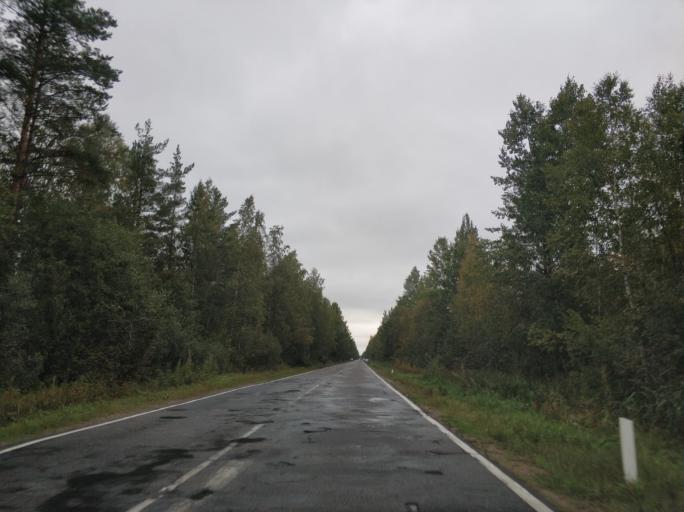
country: RU
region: Leningrad
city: Borisova Griva
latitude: 60.1639
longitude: 30.9213
